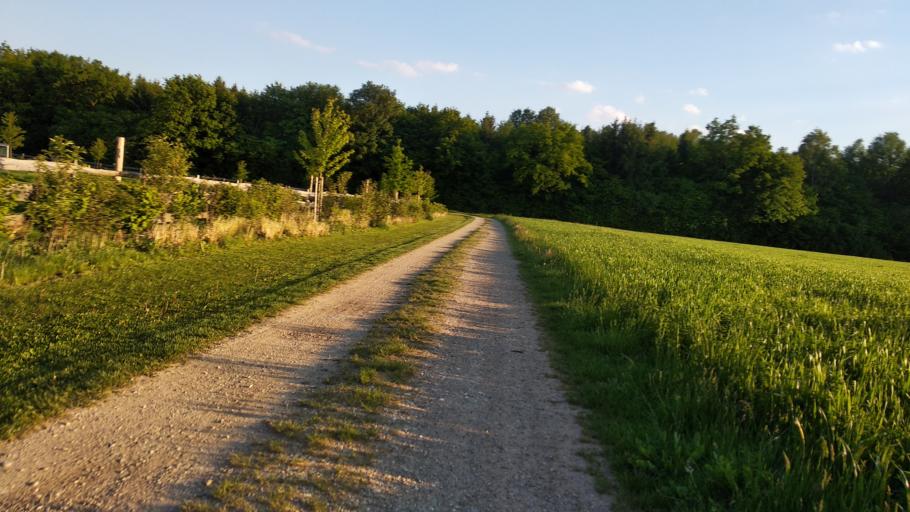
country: DE
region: Bavaria
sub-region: Upper Bavaria
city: Zorneding
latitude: 48.0908
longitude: 11.8029
